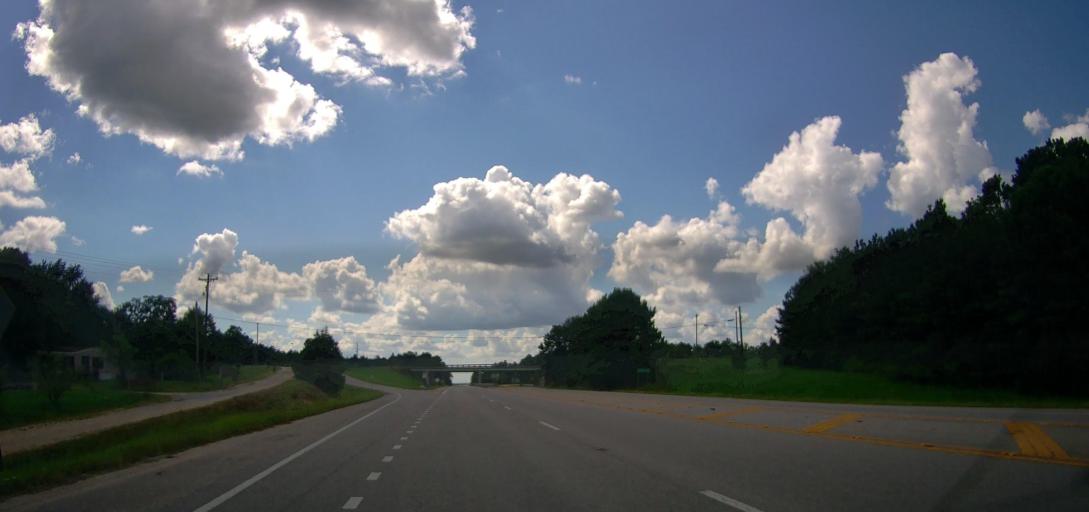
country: US
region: Alabama
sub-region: Macon County
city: Tuskegee
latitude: 32.4676
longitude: -85.5747
